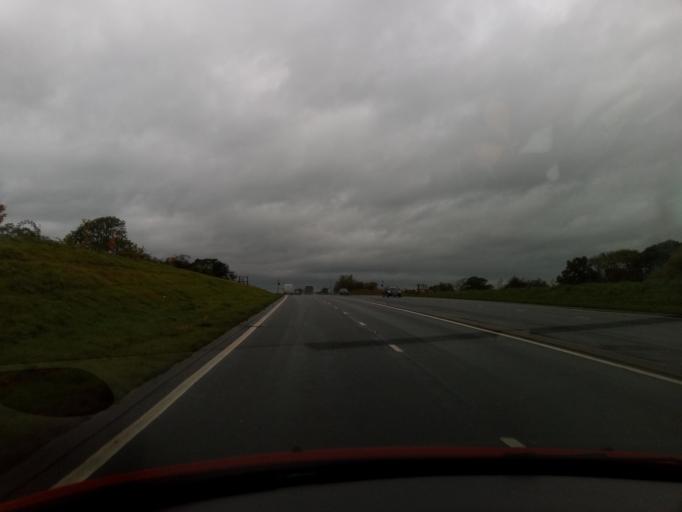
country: GB
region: England
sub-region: Lancashire
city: Preston
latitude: 53.8068
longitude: -2.7138
